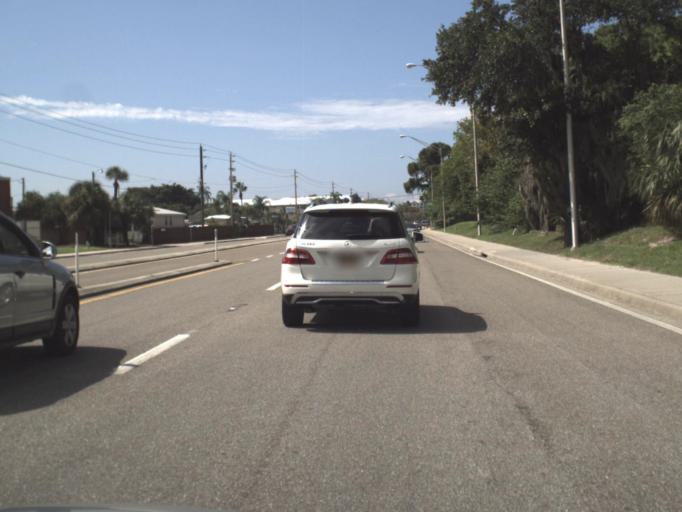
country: US
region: Florida
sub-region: Sarasota County
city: Gulf Gate Estates
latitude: 27.2595
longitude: -82.5241
